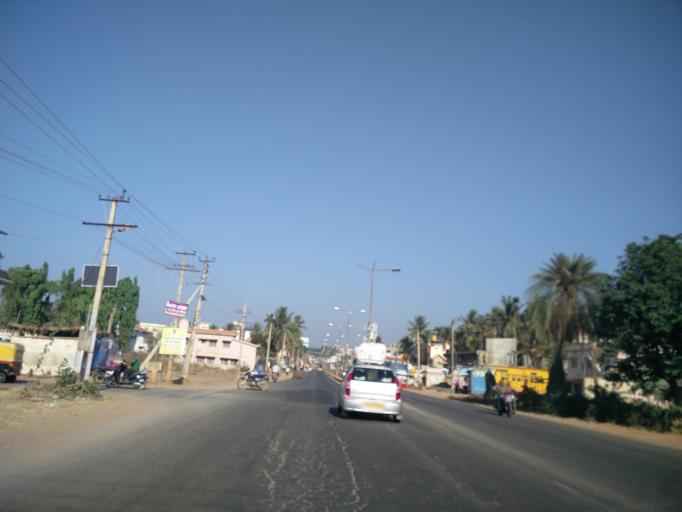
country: IN
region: Karnataka
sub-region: Tumkur
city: Gubbi
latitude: 13.3091
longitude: 76.9475
